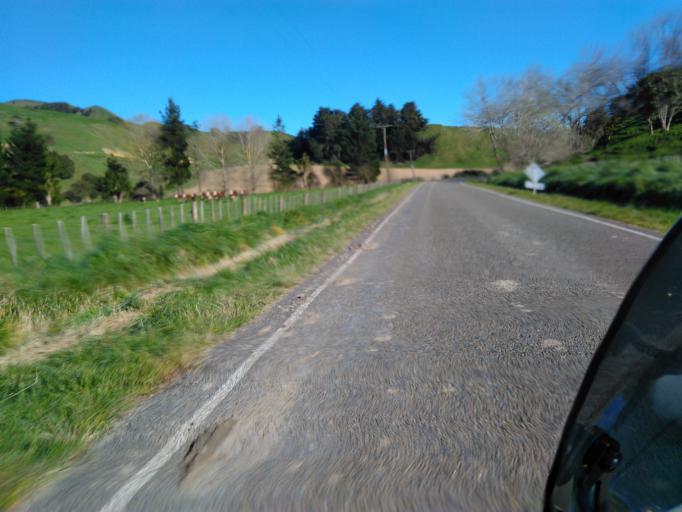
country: NZ
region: Gisborne
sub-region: Gisborne District
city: Gisborne
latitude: -38.4367
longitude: 177.7434
